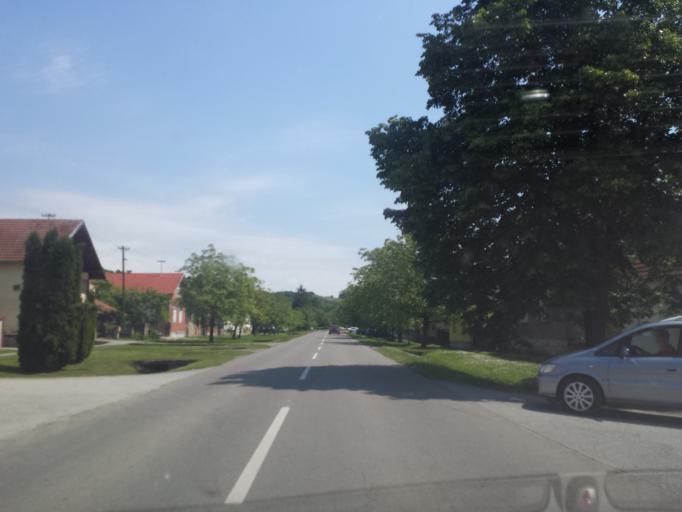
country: HR
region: Brodsko-Posavska
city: Luzani
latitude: 45.1715
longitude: 17.7249
